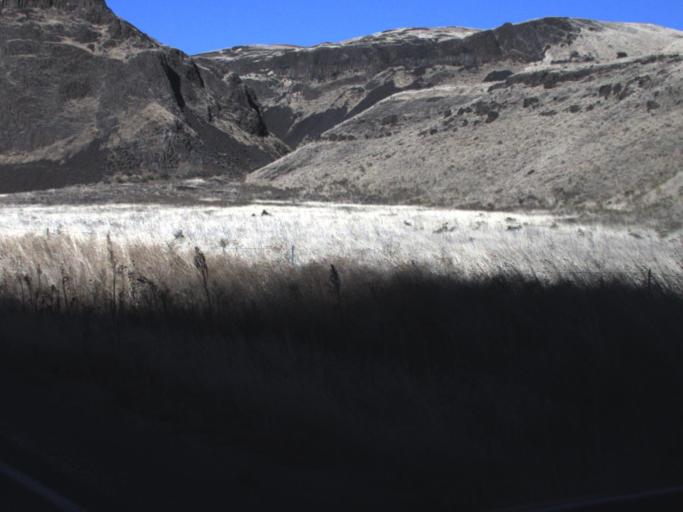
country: US
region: Washington
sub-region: Franklin County
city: Connell
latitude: 46.5913
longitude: -118.5453
